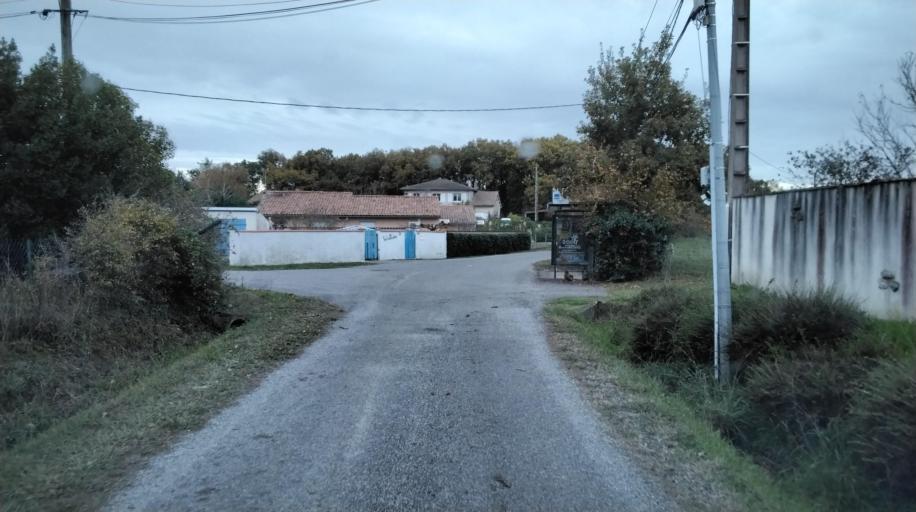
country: FR
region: Midi-Pyrenees
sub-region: Departement de la Haute-Garonne
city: Berat
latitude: 43.3932
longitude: 1.2051
